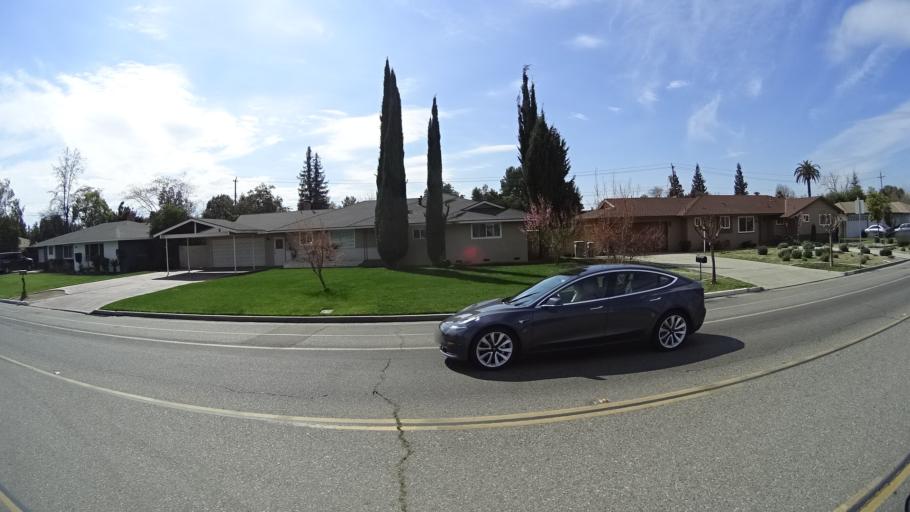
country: US
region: California
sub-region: Fresno County
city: Fresno
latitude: 36.8157
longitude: -119.8105
